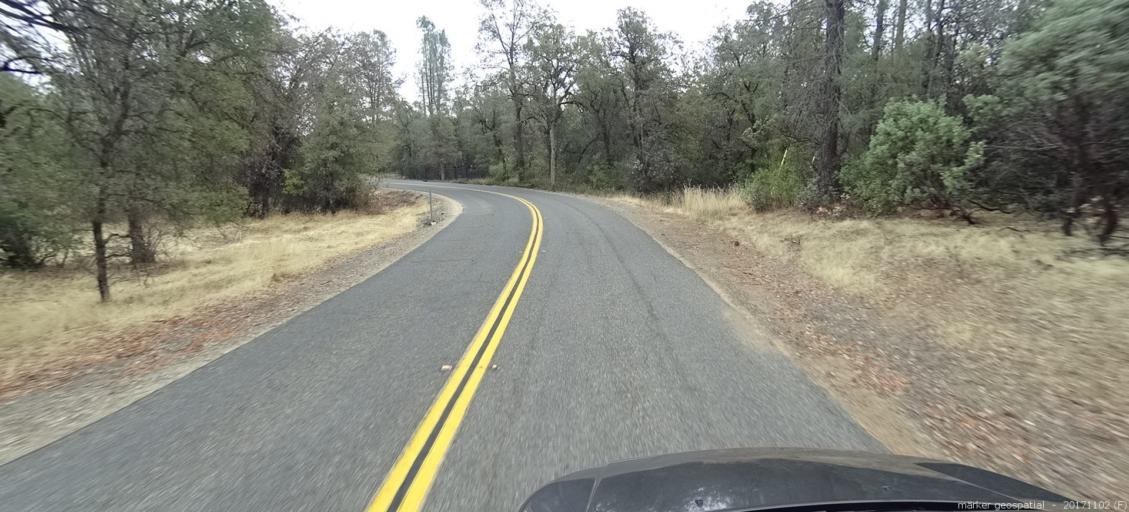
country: US
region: California
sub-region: Shasta County
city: Redding
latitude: 40.6364
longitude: -122.4273
